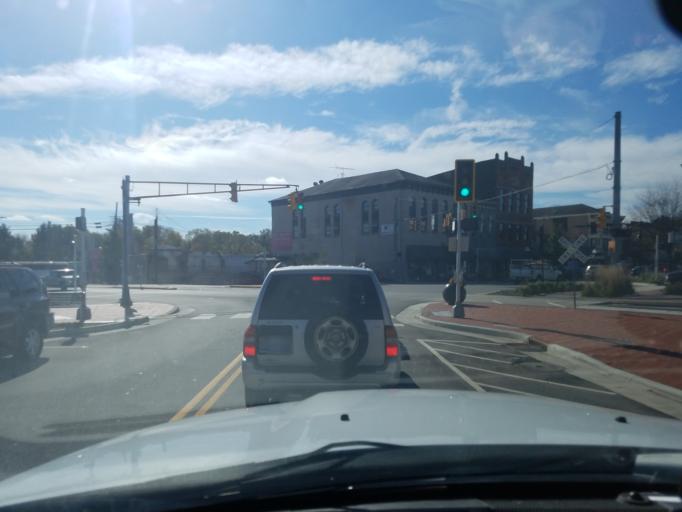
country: US
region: Indiana
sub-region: Jennings County
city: North Vernon
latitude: 39.0063
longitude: -85.6237
